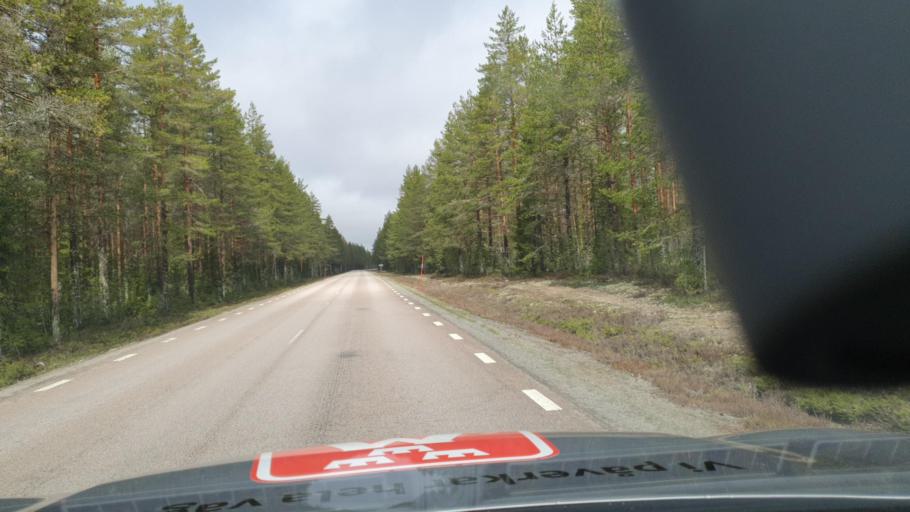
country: SE
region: Vaesternorrland
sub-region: OErnskoeldsviks Kommun
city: Husum
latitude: 63.4227
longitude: 18.9627
